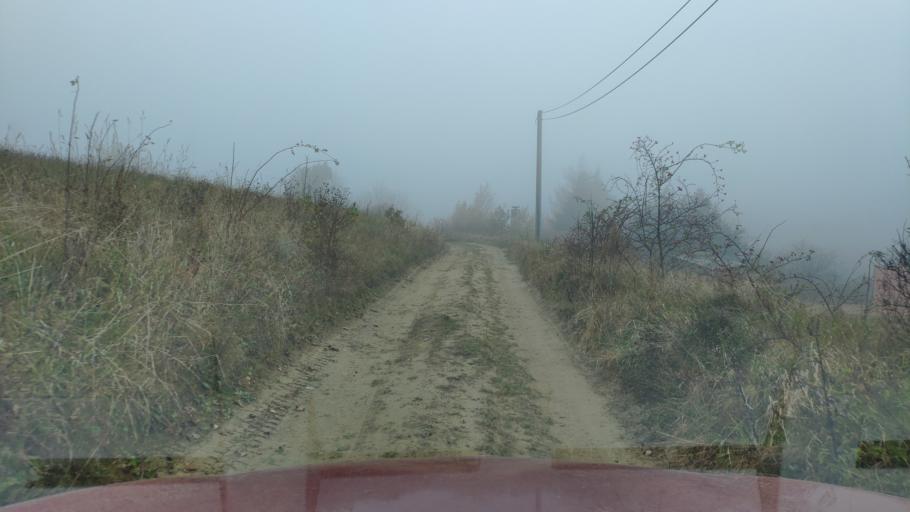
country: SK
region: Presovsky
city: Sabinov
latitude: 49.1377
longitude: 21.2281
